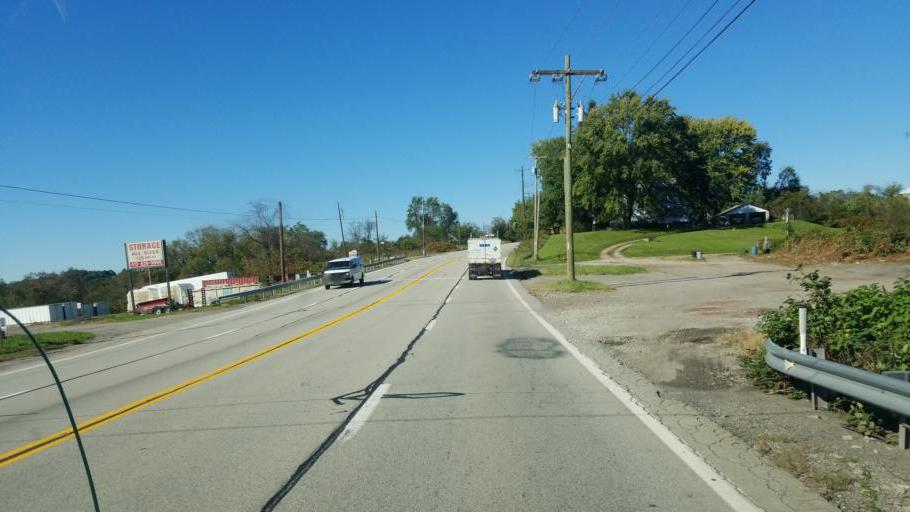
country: US
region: Pennsylvania
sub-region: Westmoreland County
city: Trafford
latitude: 40.3489
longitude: -79.7668
